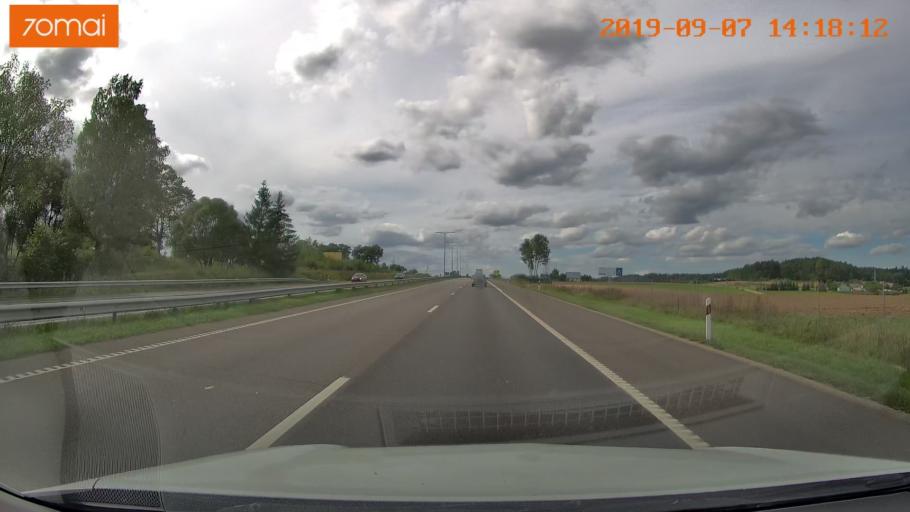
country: LT
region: Vilnius County
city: Elektrenai
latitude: 54.7965
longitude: 24.5655
